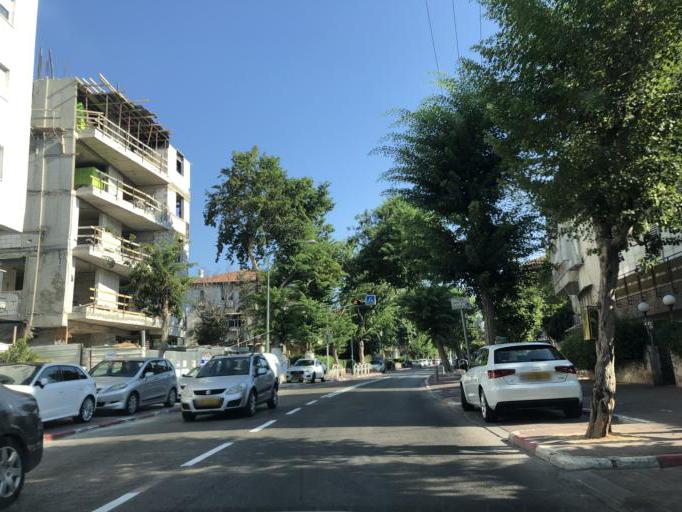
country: IL
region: Tel Aviv
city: Bene Beraq
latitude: 32.0820
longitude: 34.8256
